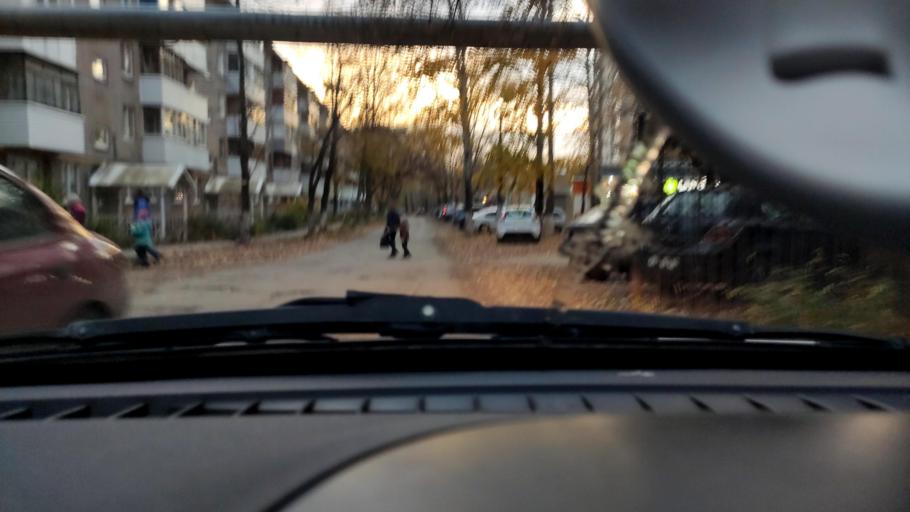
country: RU
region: Perm
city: Perm
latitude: 57.9800
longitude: 56.2928
